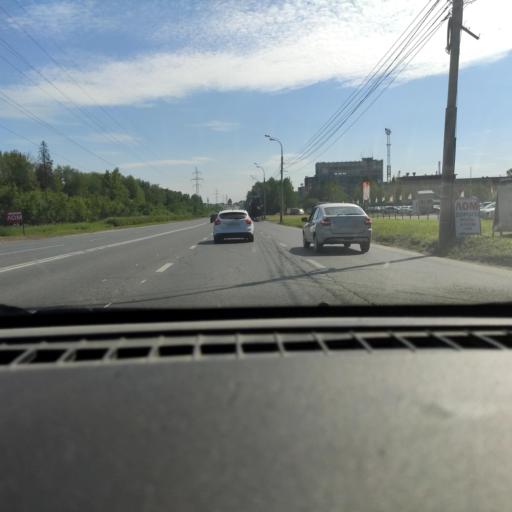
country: RU
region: Udmurtiya
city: Khokhryaki
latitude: 56.8961
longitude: 53.2906
